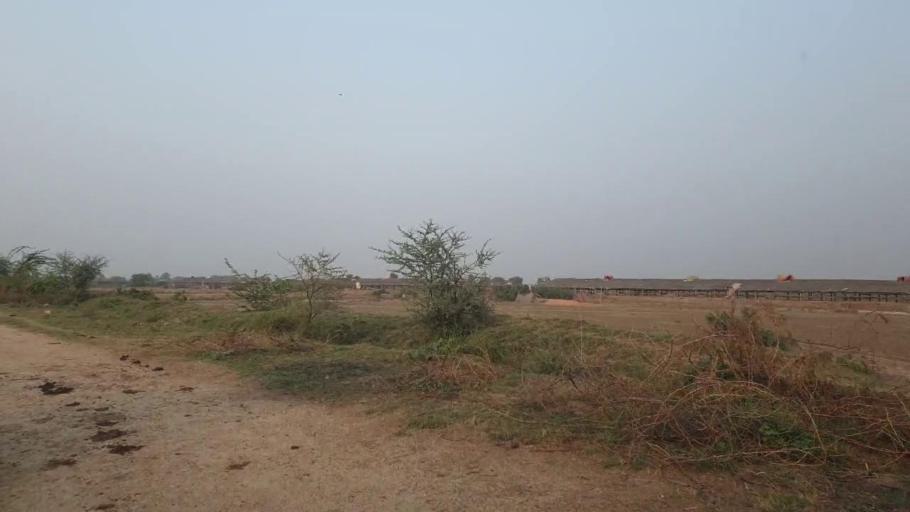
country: PK
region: Sindh
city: Mirpur Batoro
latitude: 24.6517
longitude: 68.3784
